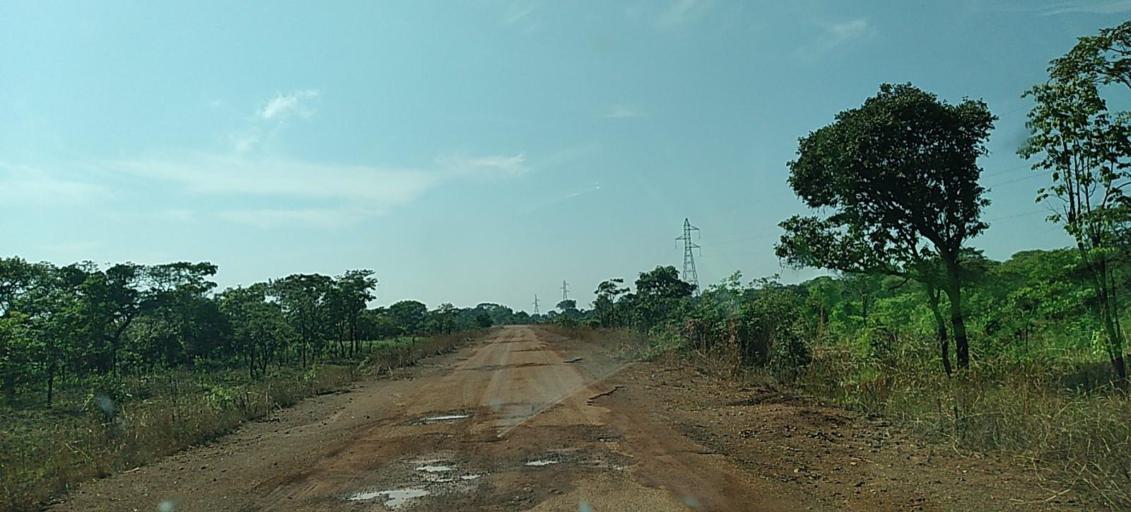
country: ZM
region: North-Western
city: Mwinilunga
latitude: -11.8181
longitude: 25.0933
